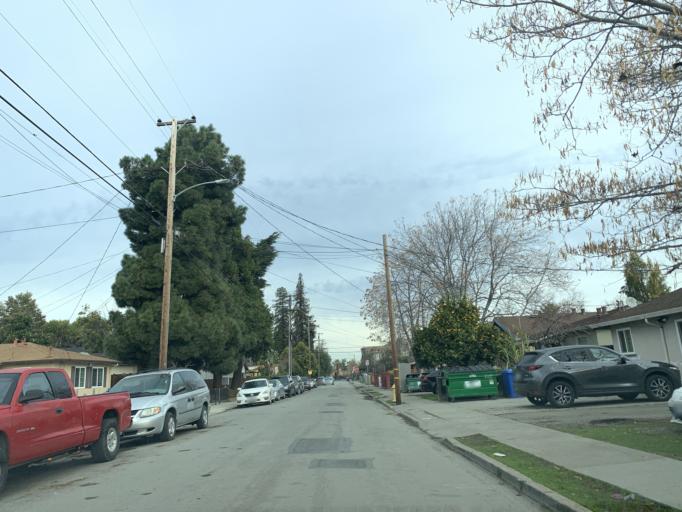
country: US
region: California
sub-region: Santa Clara County
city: Buena Vista
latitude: 37.3206
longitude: -121.9155
